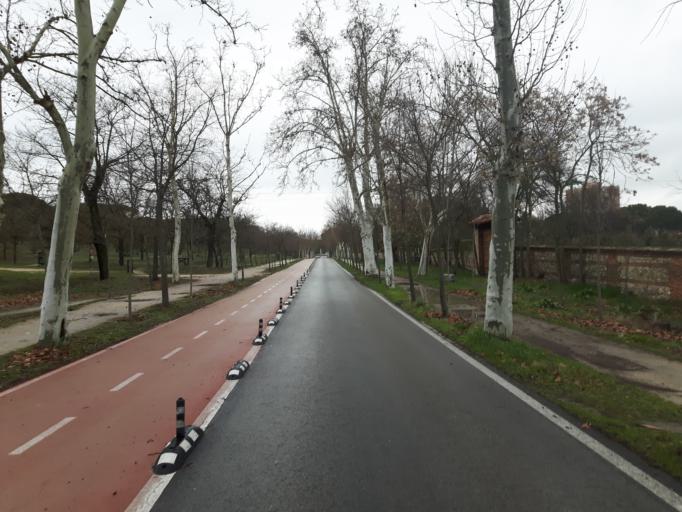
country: ES
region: Madrid
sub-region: Provincia de Madrid
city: Moncloa-Aravaca
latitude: 40.4224
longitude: -3.7312
